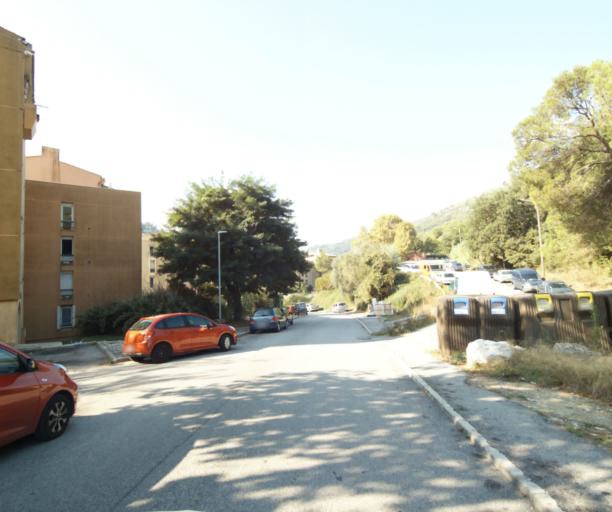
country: FR
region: Provence-Alpes-Cote d'Azur
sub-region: Departement des Alpes-Maritimes
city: Cantaron
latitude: 43.7716
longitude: 7.3316
